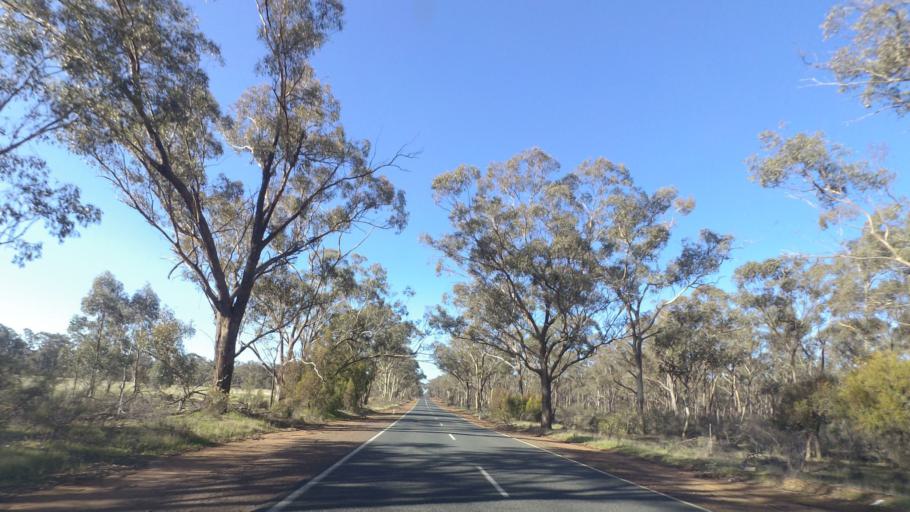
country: AU
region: Victoria
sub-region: Greater Bendigo
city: Epsom
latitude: -36.6698
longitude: 144.4203
